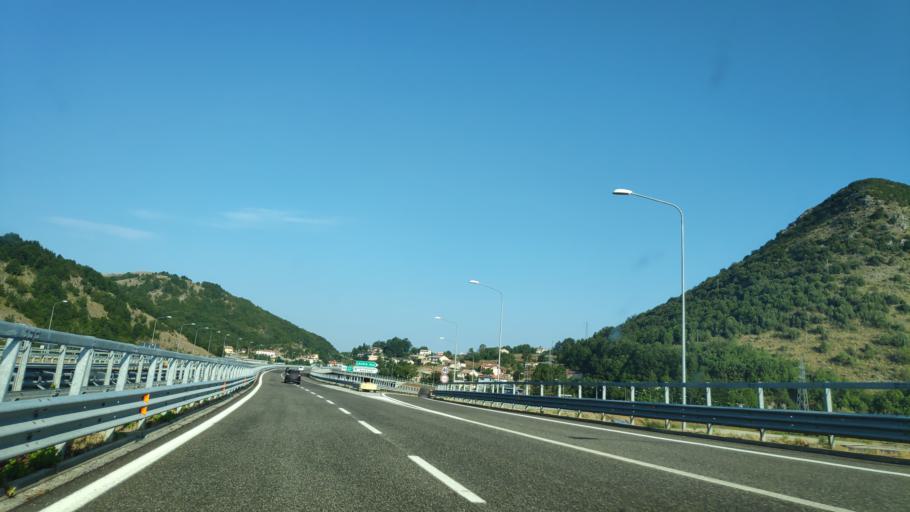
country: IT
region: Basilicate
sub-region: Provincia di Potenza
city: Lauria
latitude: 40.0174
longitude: 15.8904
